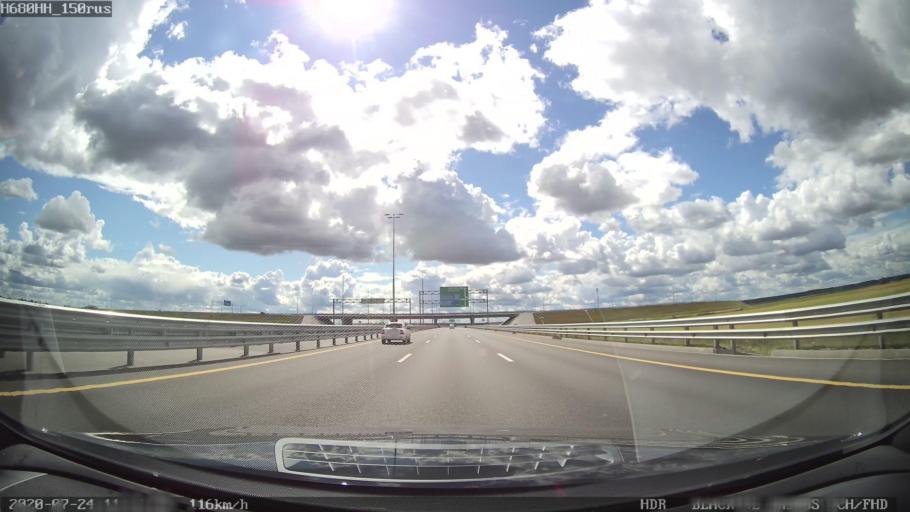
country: RU
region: St.-Petersburg
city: Tyarlevo
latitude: 59.7300
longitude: 30.5098
